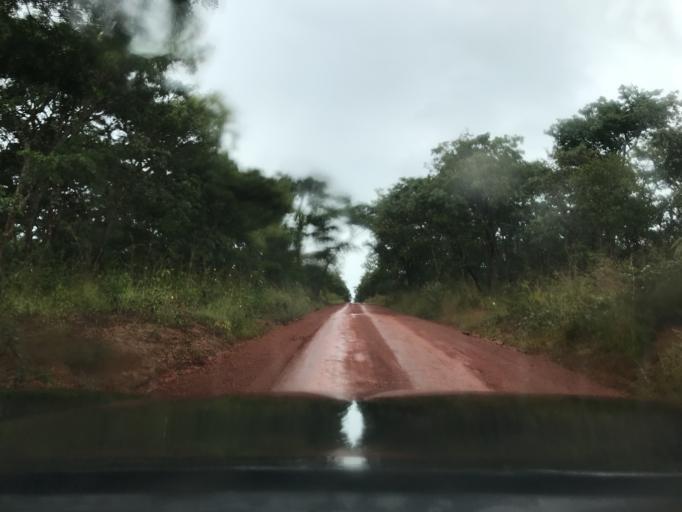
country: TZ
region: Kigoma
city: Uvinza
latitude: -5.2969
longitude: 30.3767
